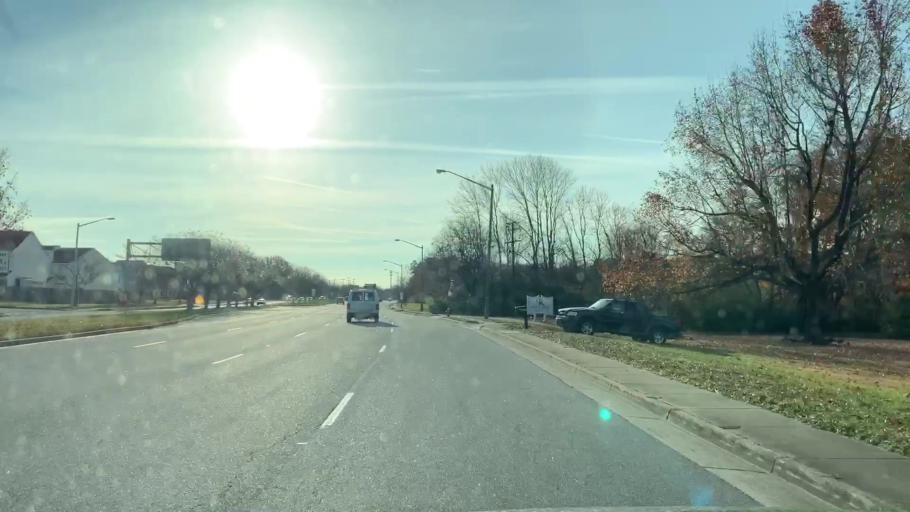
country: US
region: Virginia
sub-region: City of Chesapeake
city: Chesapeake
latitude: 36.7884
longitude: -76.1637
